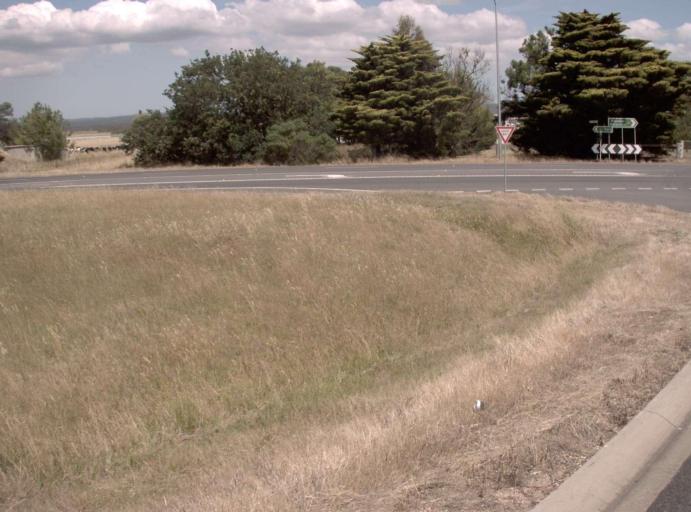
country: AU
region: Victoria
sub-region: Wellington
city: Heyfield
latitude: -38.1188
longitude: 146.8604
